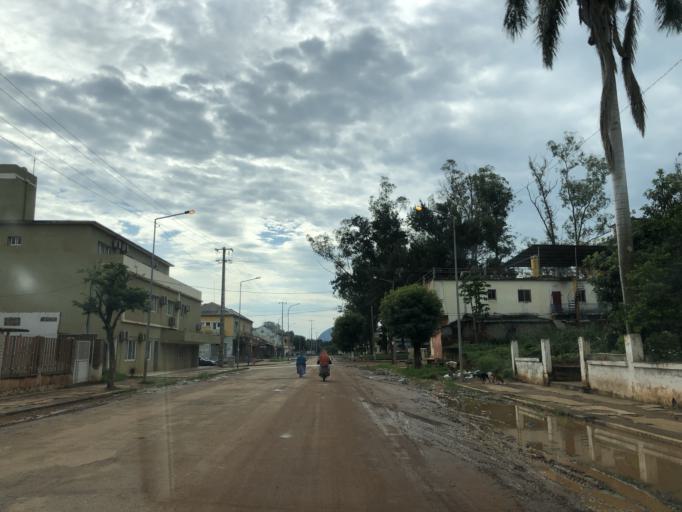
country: AO
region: Cuanza Sul
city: Uacu Cungo
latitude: -11.3642
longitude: 15.1170
